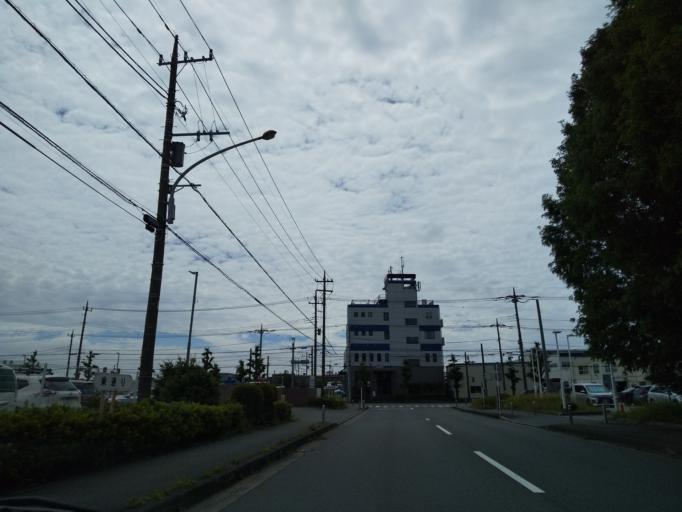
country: JP
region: Kanagawa
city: Zama
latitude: 35.5106
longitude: 139.3549
